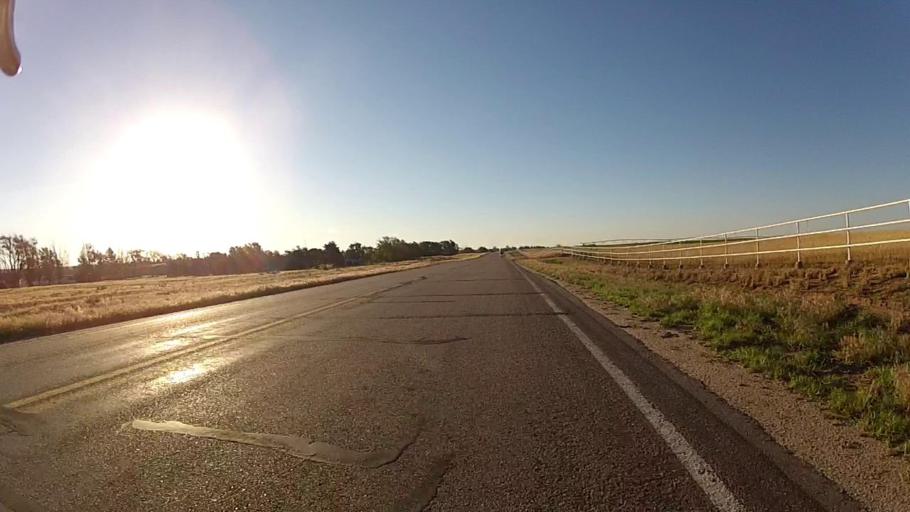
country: US
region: Kansas
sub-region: Ford County
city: Dodge City
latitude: 37.7204
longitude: -99.9499
